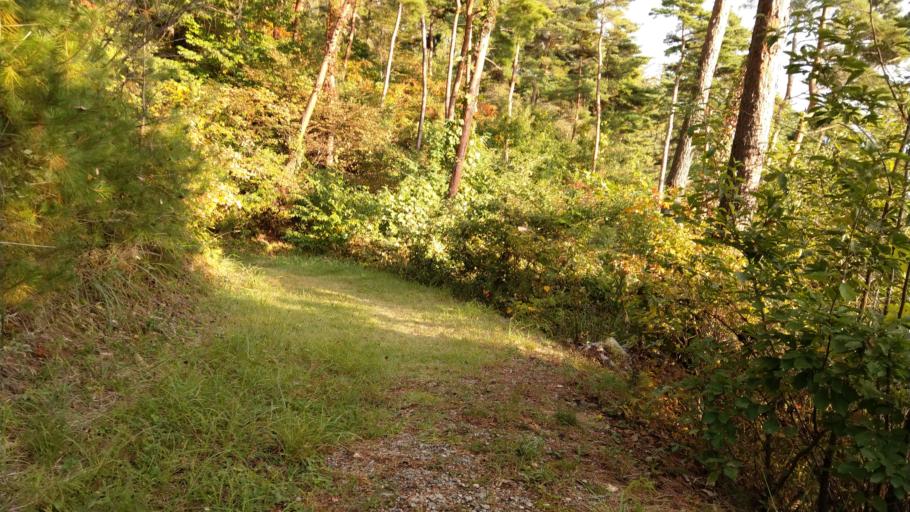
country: JP
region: Nagano
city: Komoro
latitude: 36.3436
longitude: 138.4185
